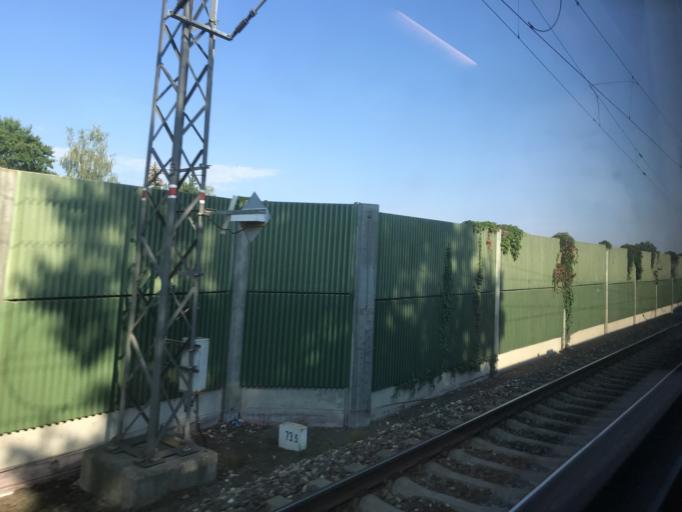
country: CZ
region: Jihocesky
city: Plana nad Luznici
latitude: 49.3448
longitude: 14.7101
